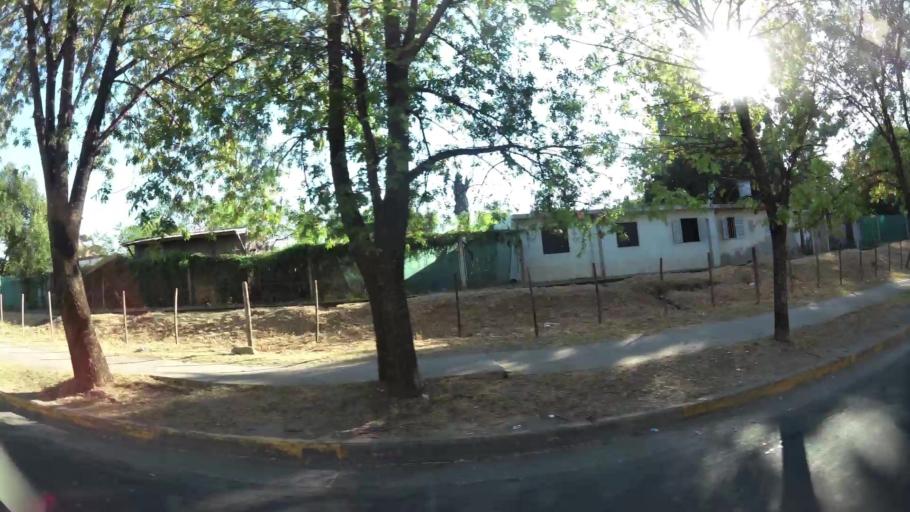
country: AR
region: Cordoba
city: Villa Allende
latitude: -31.3411
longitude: -64.2546
